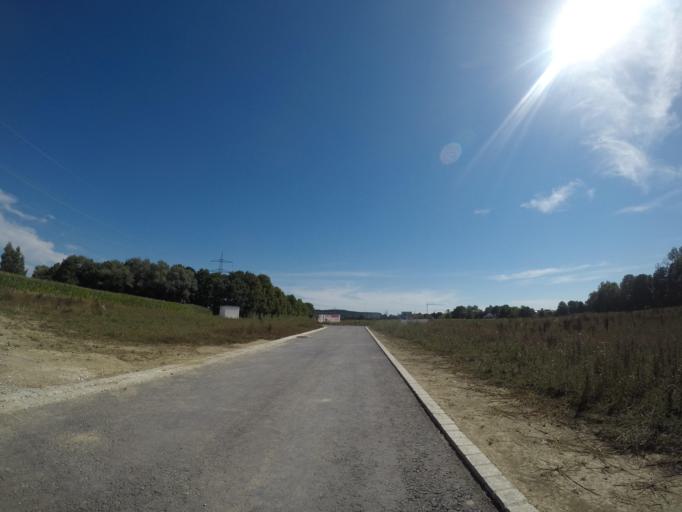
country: DE
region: Bavaria
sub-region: Swabia
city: Senden
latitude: 48.3317
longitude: 10.0242
